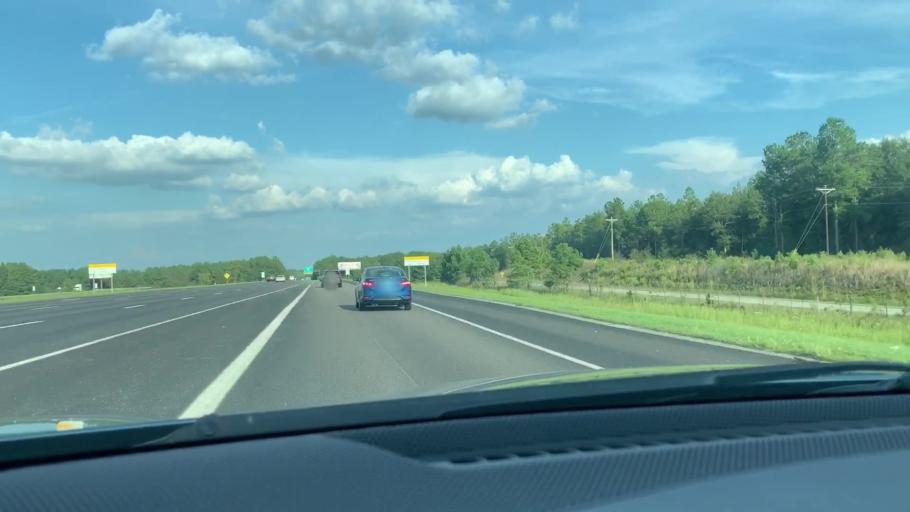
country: US
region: South Carolina
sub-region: Lexington County
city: Cayce
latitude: 33.9282
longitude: -81.0618
